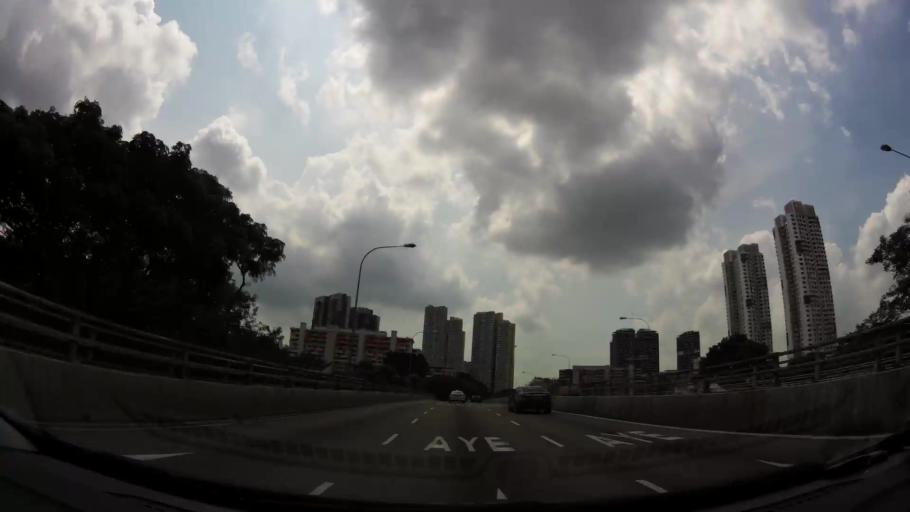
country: SG
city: Singapore
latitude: 1.3243
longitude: 103.7643
